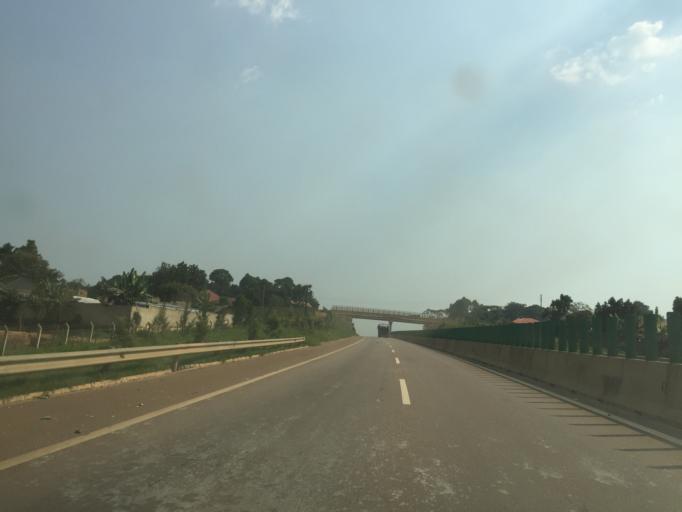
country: UG
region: Central Region
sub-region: Wakiso District
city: Kajansi
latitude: 0.2495
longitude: 32.5227
